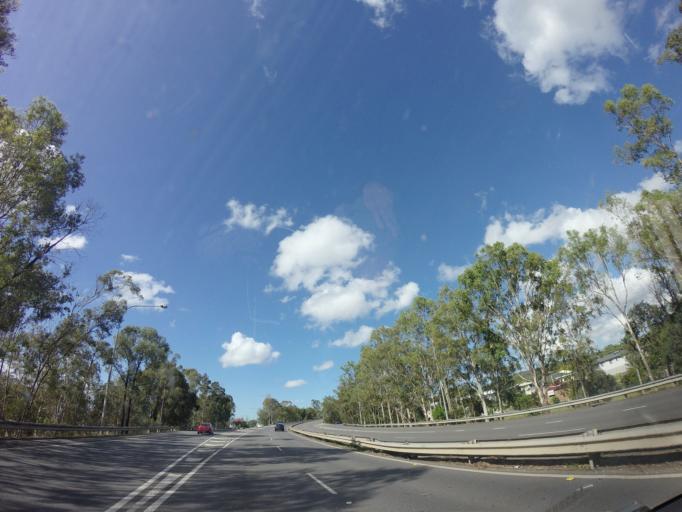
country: AU
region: Queensland
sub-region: Brisbane
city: Rocklea
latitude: -27.5458
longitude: 153.0102
